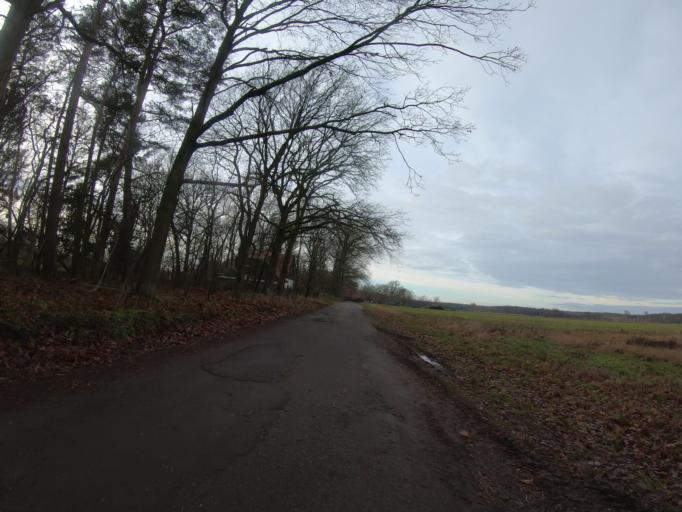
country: DE
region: Lower Saxony
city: Muden
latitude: 52.5100
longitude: 10.4139
